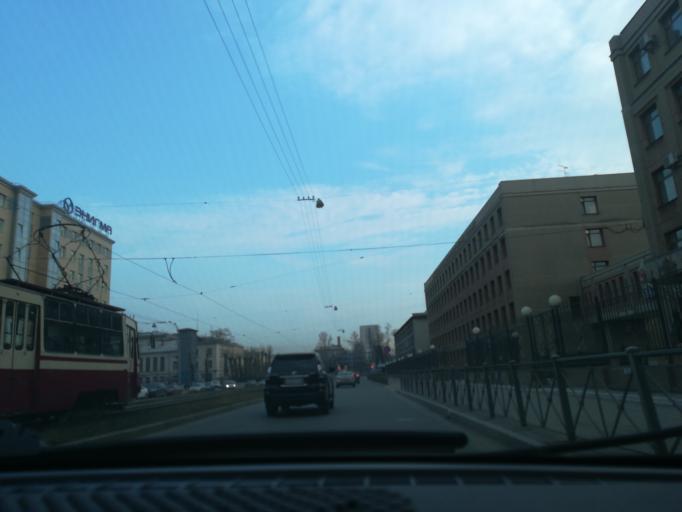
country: RU
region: St.-Petersburg
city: Avtovo
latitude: 59.8748
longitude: 30.2541
